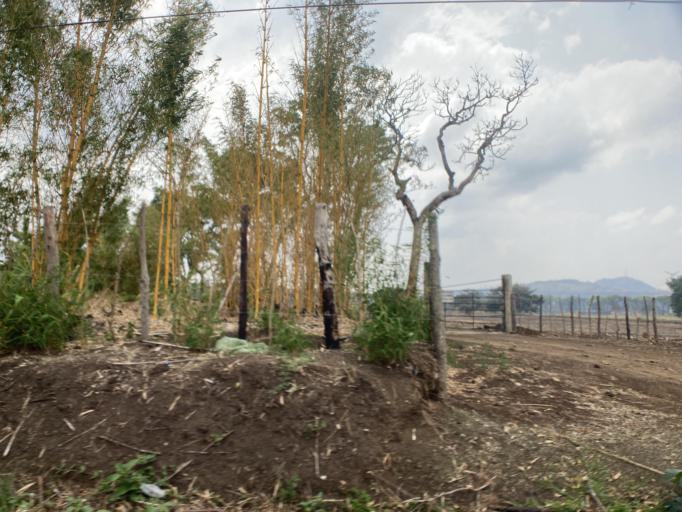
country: GT
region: Guatemala
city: Fraijanes
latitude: 14.3934
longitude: -90.4829
